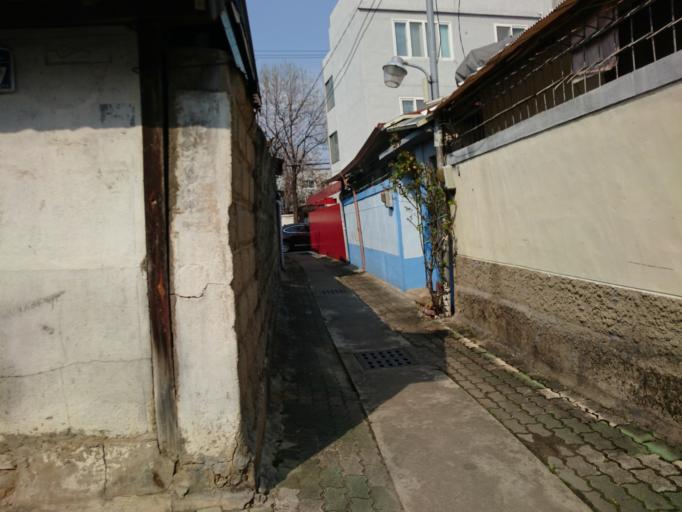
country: KR
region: Daegu
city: Daegu
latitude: 35.8604
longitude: 128.6061
